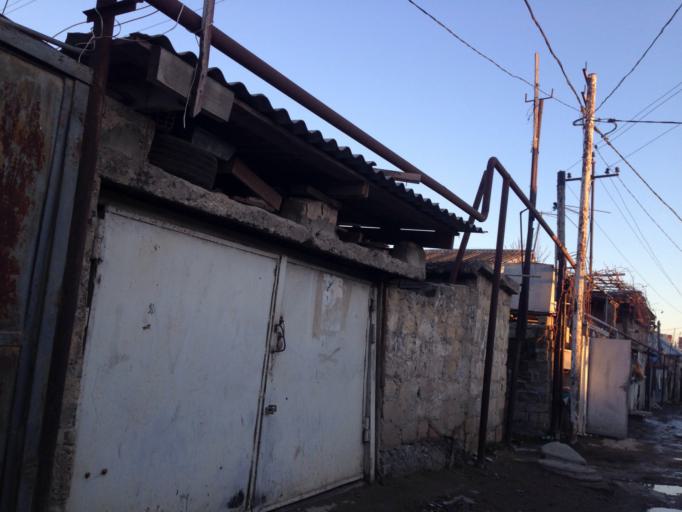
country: AZ
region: Baki
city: Baku
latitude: 40.4161
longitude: 49.8655
